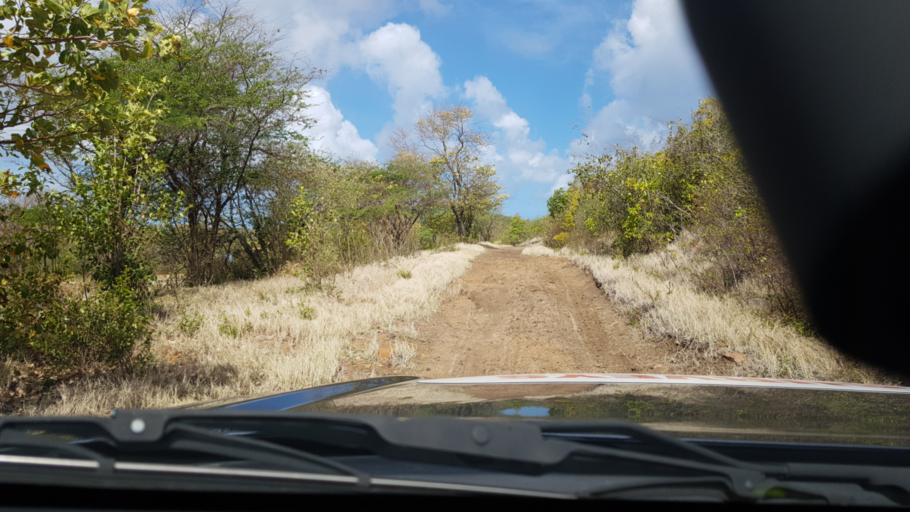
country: LC
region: Gros-Islet
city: Gros Islet
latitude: 14.0816
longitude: -60.9259
